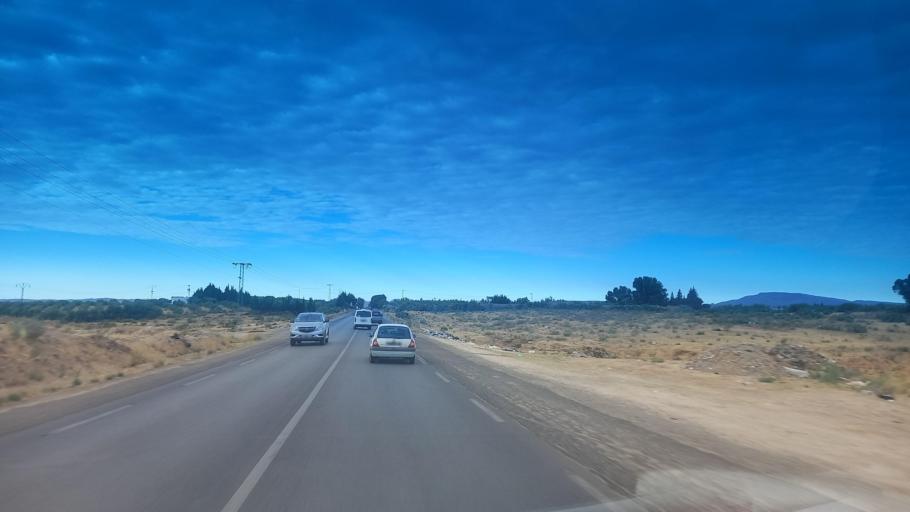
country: TN
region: Al Qasrayn
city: Sbiba
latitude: 35.2796
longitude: 9.0939
